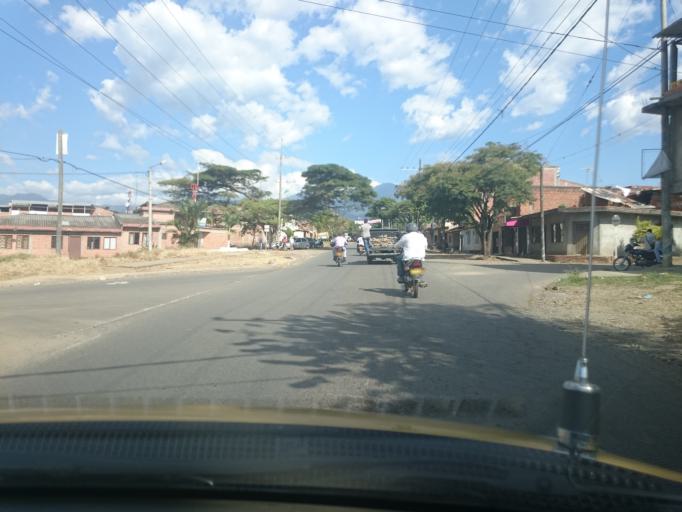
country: CO
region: Cauca
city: Santander de Quilichao
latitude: 3.0123
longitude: -76.4892
